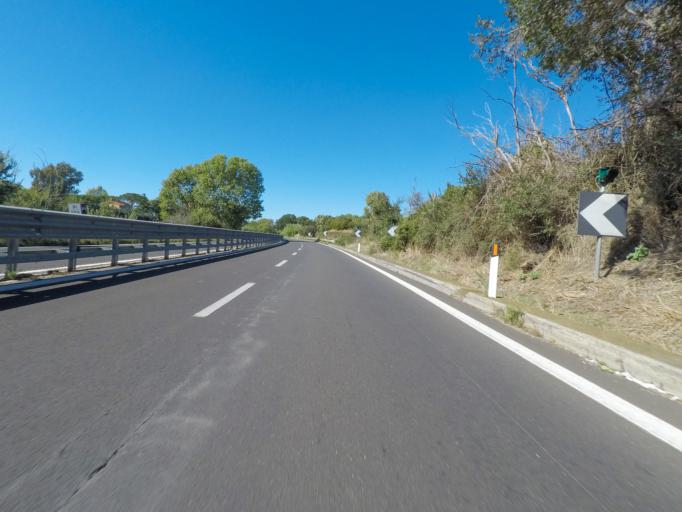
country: IT
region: Latium
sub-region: Provincia di Viterbo
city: Montalto di Castro
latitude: 42.3198
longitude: 11.6495
